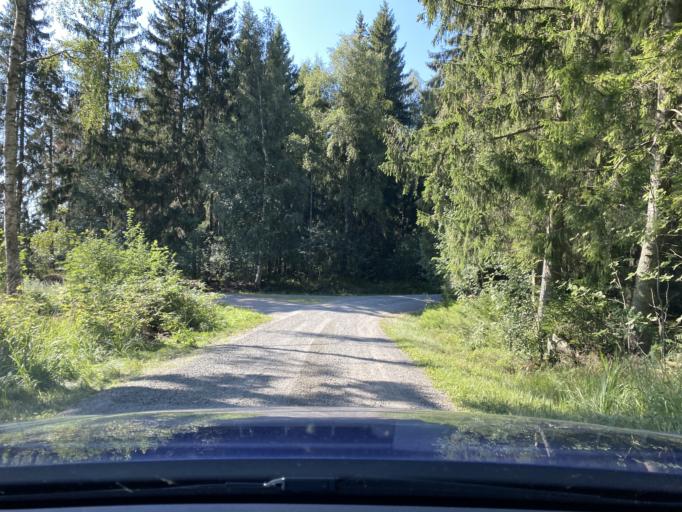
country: FI
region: Satakunta
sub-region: Rauma
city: Kiukainen
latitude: 61.1462
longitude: 22.0132
